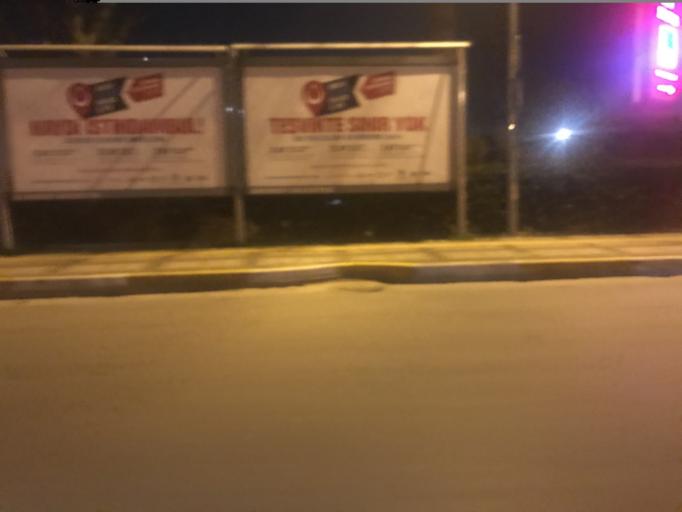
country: TR
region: Istanbul
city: Bahcelievler
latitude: 40.9598
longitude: 28.8381
